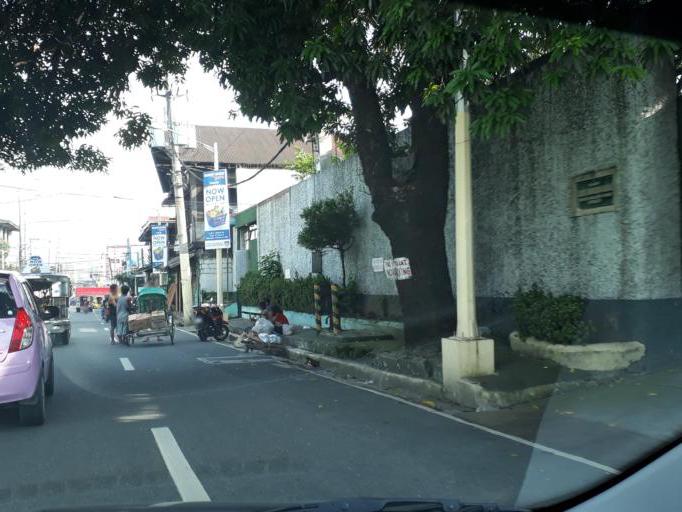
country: PH
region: Metro Manila
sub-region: Caloocan City
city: Niugan
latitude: 14.6466
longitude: 120.9740
